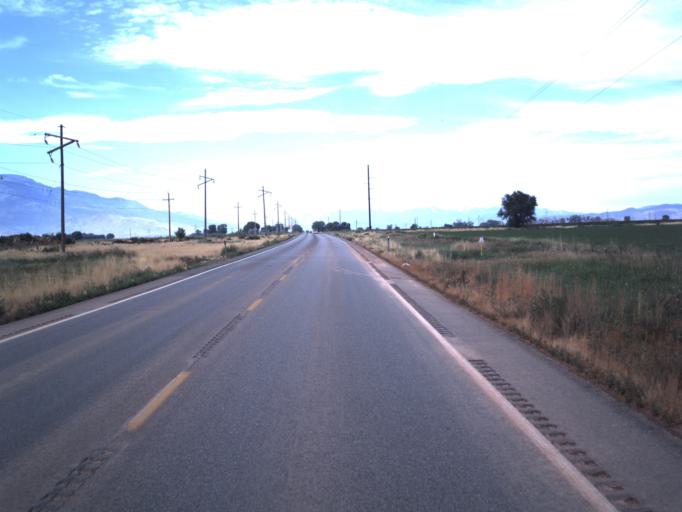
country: US
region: Utah
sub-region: Sevier County
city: Aurora
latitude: 38.8544
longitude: -111.9732
